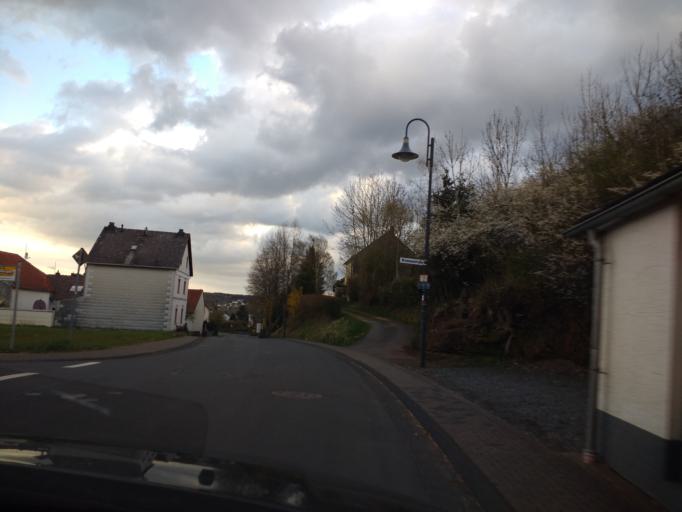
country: DE
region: Rheinland-Pfalz
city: Lissendorf
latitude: 50.3153
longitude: 6.6083
